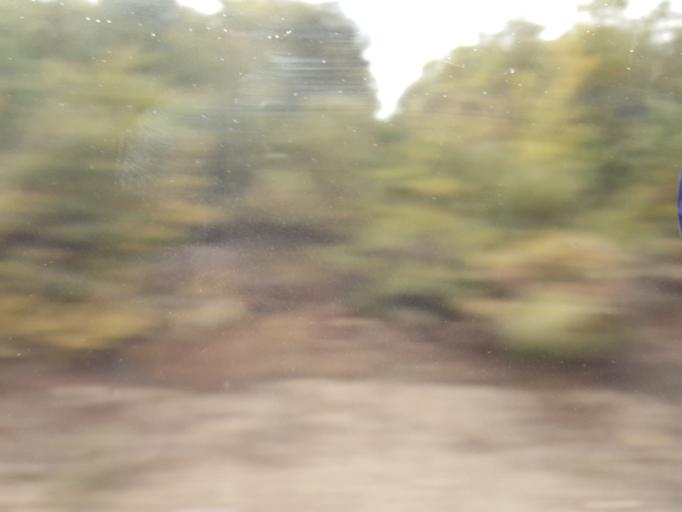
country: TR
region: Amasya
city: Gediksaray
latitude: 40.4441
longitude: 35.7797
